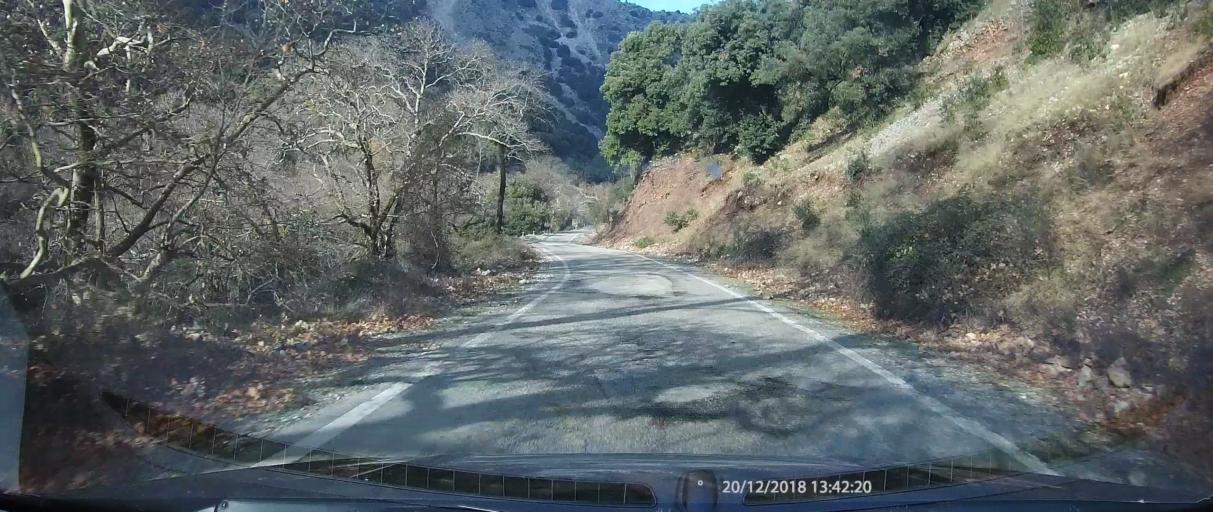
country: GR
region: West Greece
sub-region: Nomos Aitolias kai Akarnanias
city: Thermo
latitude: 38.6529
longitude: 21.6187
